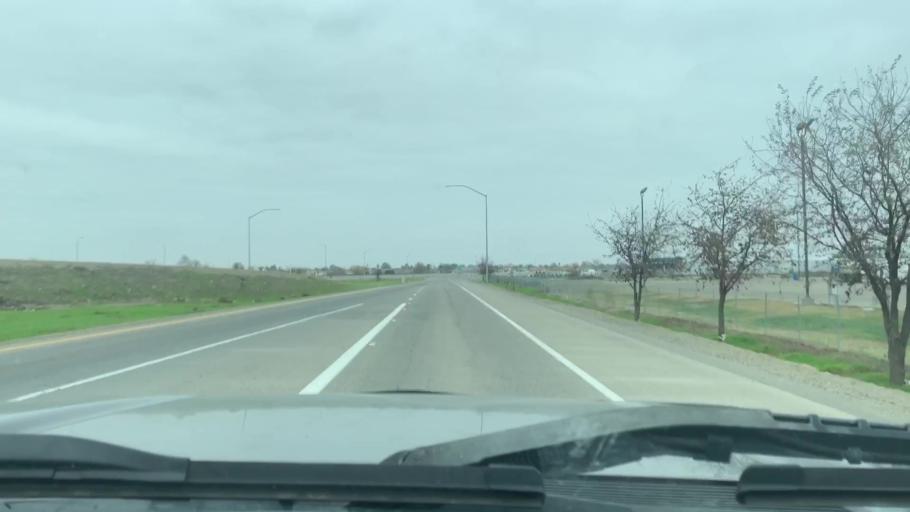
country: US
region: California
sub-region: Kings County
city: Lemoore
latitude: 36.2806
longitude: -119.8071
